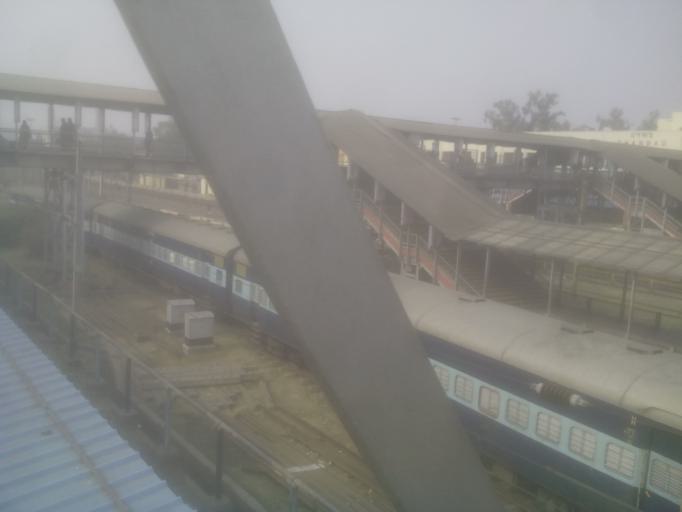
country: IN
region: Jharkhand
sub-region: Dhanbad
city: Dhanbad
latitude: 23.7915
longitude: 86.4279
